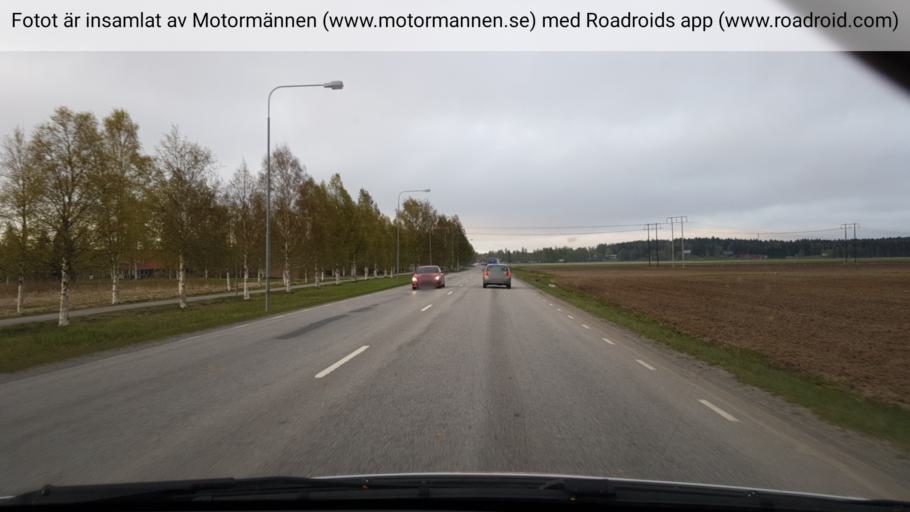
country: SE
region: Vaesterbotten
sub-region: Umea Kommun
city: Roback
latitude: 63.8118
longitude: 20.2106
